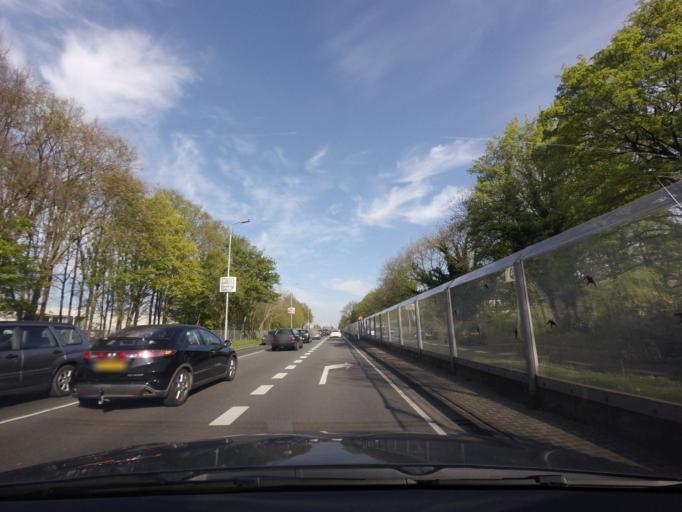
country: NL
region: North Brabant
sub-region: Gemeente Eindhoven
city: De Doornakkers
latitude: 51.4305
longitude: 5.5073
